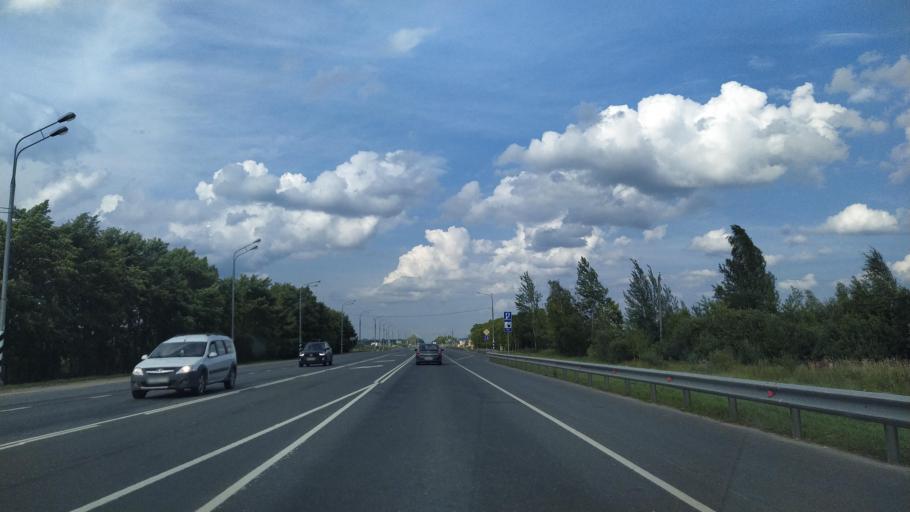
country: RU
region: Novgorod
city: Shimsk
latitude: 58.2172
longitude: 30.7335
